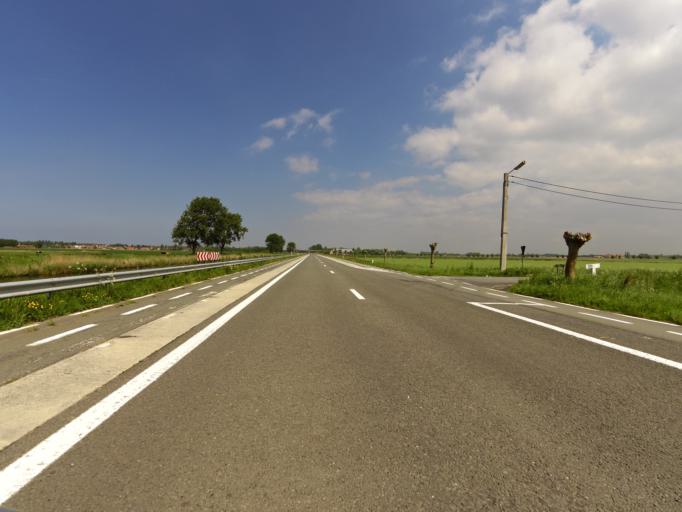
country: BE
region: Flanders
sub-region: Provincie West-Vlaanderen
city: Nieuwpoort
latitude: 51.1160
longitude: 2.7363
